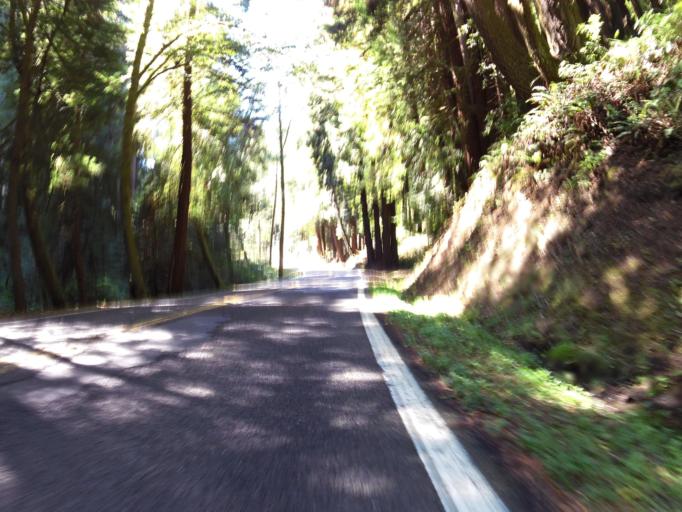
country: US
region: California
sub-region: Humboldt County
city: Redway
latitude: 39.7869
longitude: -123.8179
